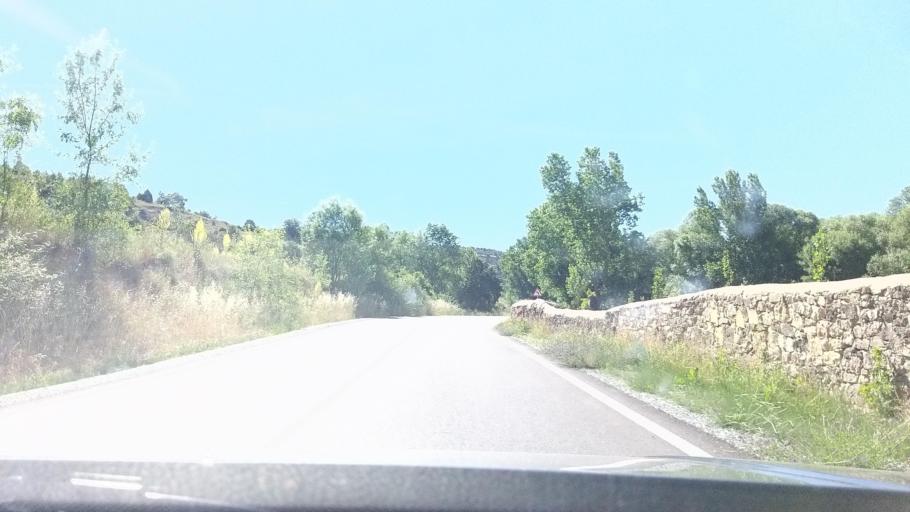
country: ES
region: Castille and Leon
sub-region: Provincia de Segovia
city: Pedraza
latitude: 41.1404
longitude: -3.8214
